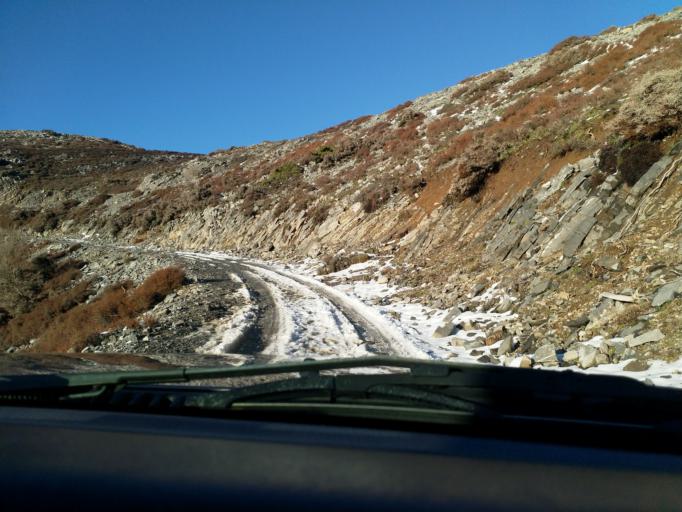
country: GR
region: Crete
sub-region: Nomos Chanias
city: Perivolia
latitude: 35.3207
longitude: 23.9292
